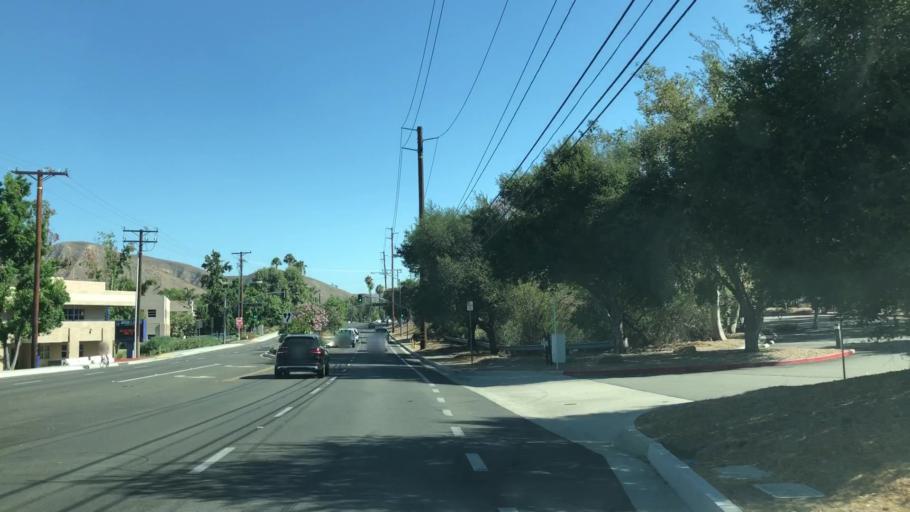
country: US
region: California
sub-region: Los Angeles County
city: Agoura
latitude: 34.1335
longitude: -118.7030
